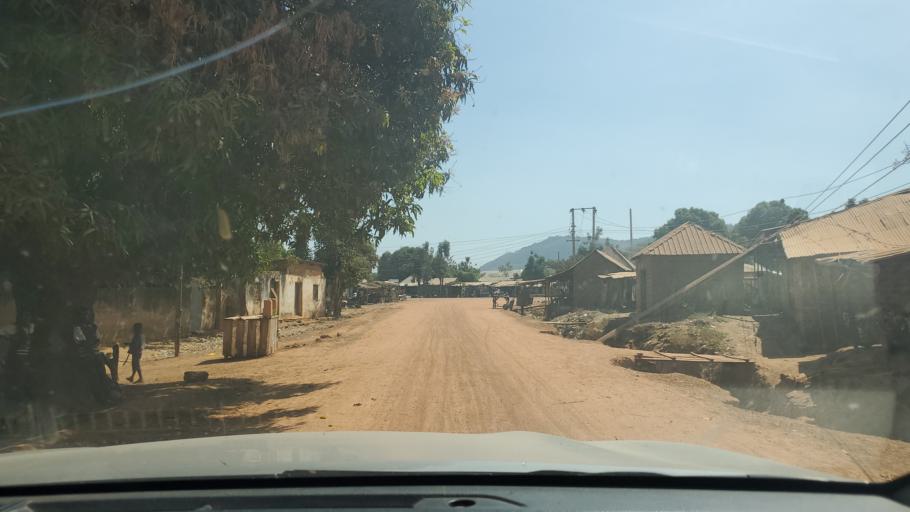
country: NG
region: Niger
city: Gawu Babangida
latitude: 9.2136
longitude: 6.8430
